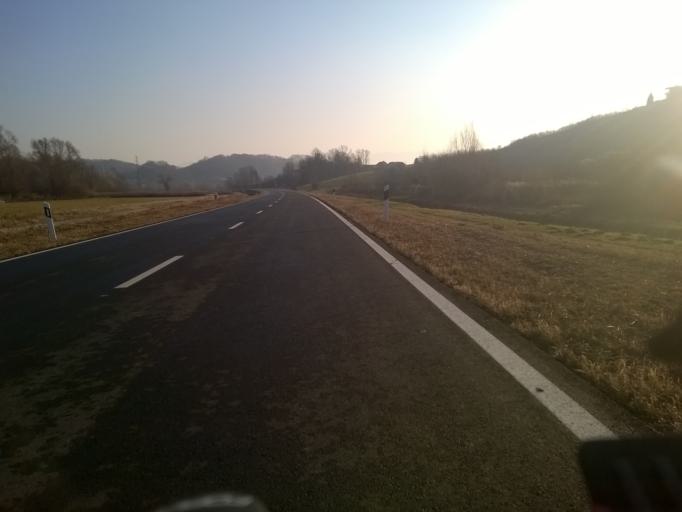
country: HR
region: Krapinsko-Zagorska
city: Zabok
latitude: 46.0411
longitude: 15.9159
